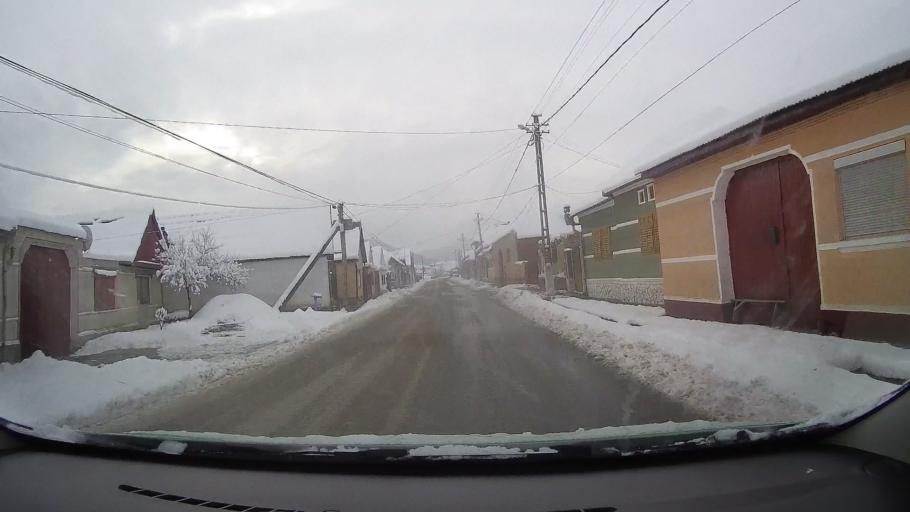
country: RO
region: Alba
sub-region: Comuna Pianu
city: Pianu de Jos
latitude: 45.9306
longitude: 23.4861
